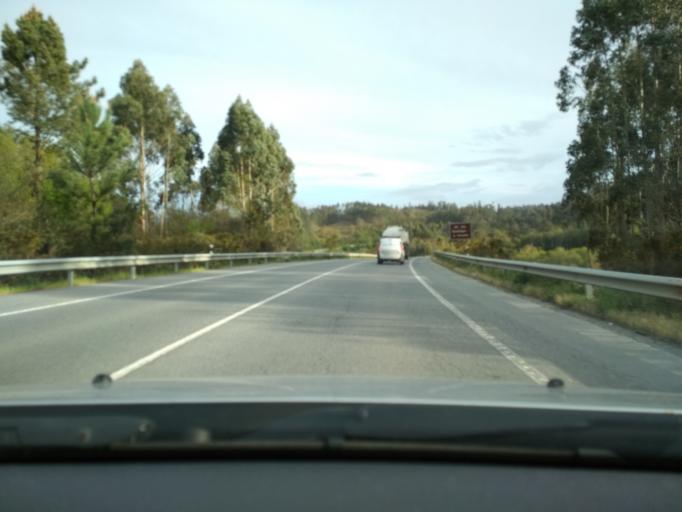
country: ES
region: Galicia
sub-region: Provincia da Coruna
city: Cerceda
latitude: 43.2221
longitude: -8.4585
